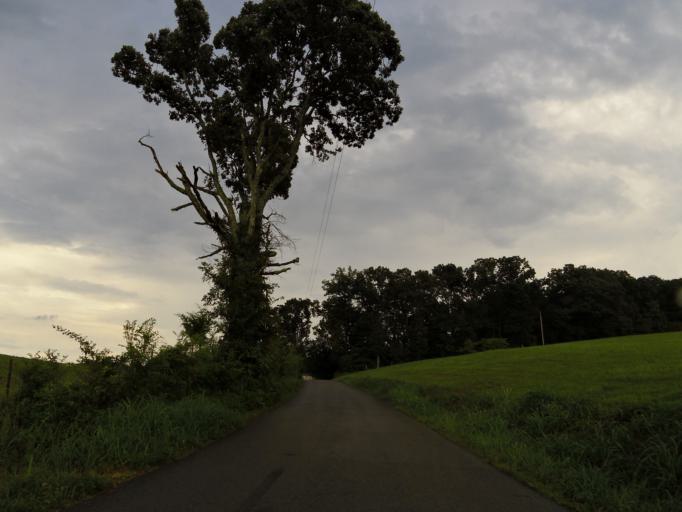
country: US
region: Tennessee
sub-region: Sevier County
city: Seymour
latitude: 35.8523
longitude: -83.7958
